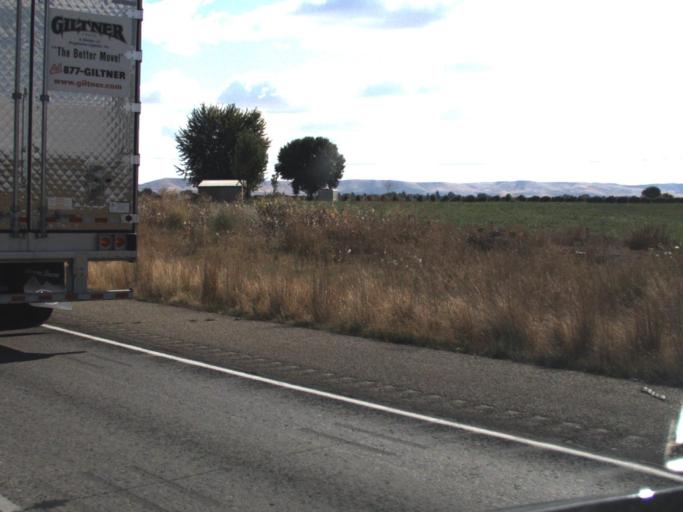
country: US
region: Washington
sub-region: Yakima County
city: Grandview
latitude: 46.2820
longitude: -119.9399
